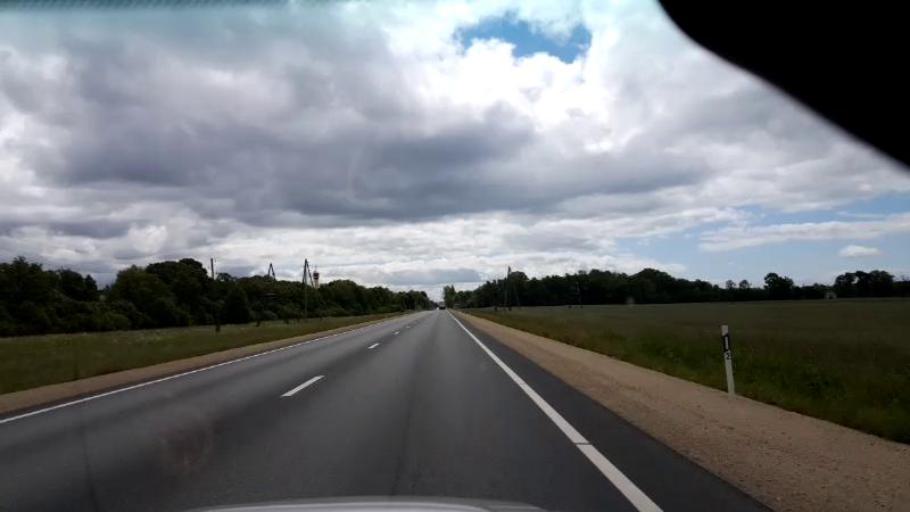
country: LV
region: Salacgrivas
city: Salacgriva
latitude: 57.7035
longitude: 24.3711
